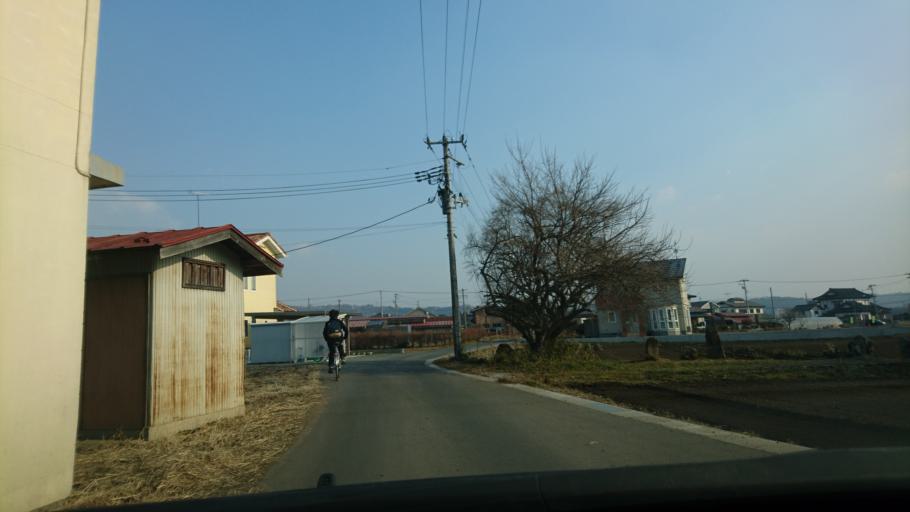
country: JP
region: Iwate
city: Ichinoseki
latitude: 38.9311
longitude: 141.0926
